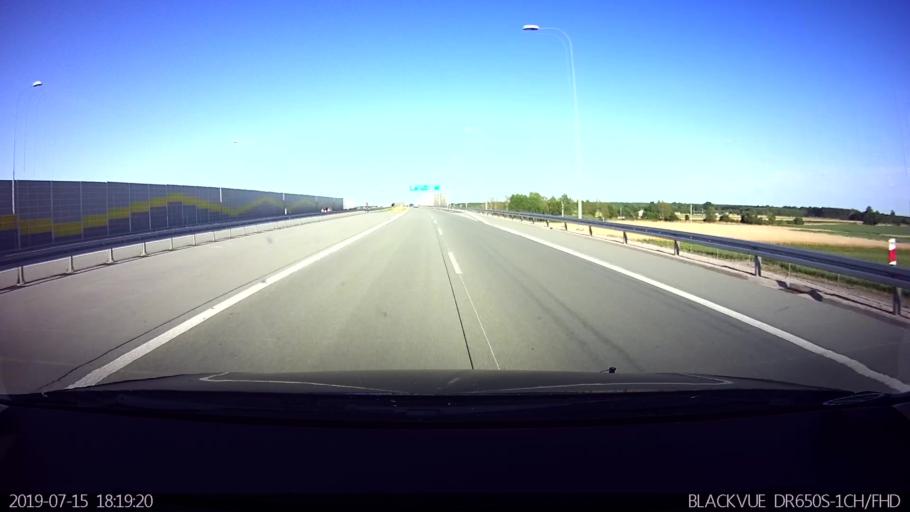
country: PL
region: Lodz Voivodeship
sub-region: Powiat laski
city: Sedziejowice
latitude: 51.5589
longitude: 19.0170
